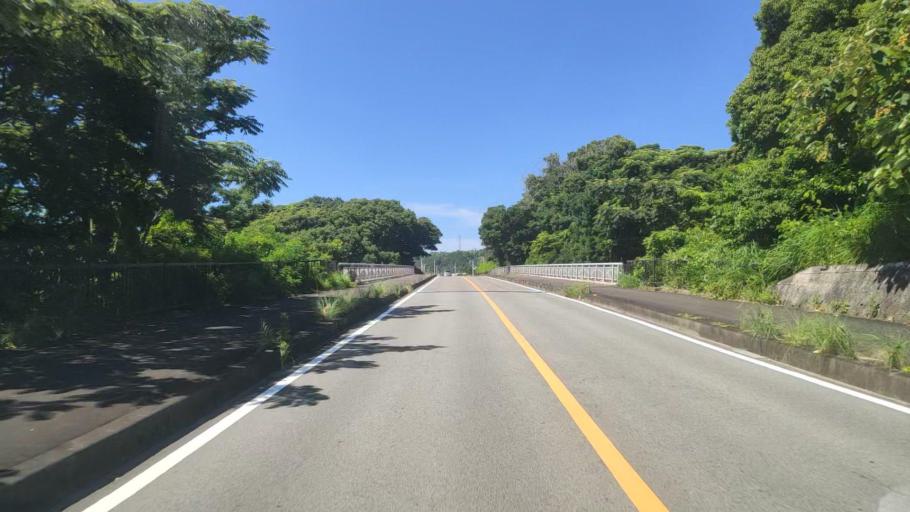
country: JP
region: Wakayama
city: Shingu
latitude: 33.7089
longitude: 135.9960
